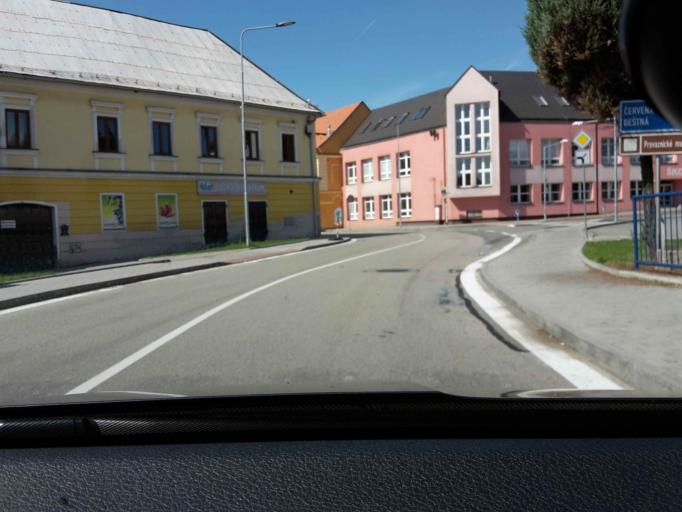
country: CZ
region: Jihocesky
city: Kardasova Recice
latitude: 49.1844
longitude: 14.8534
